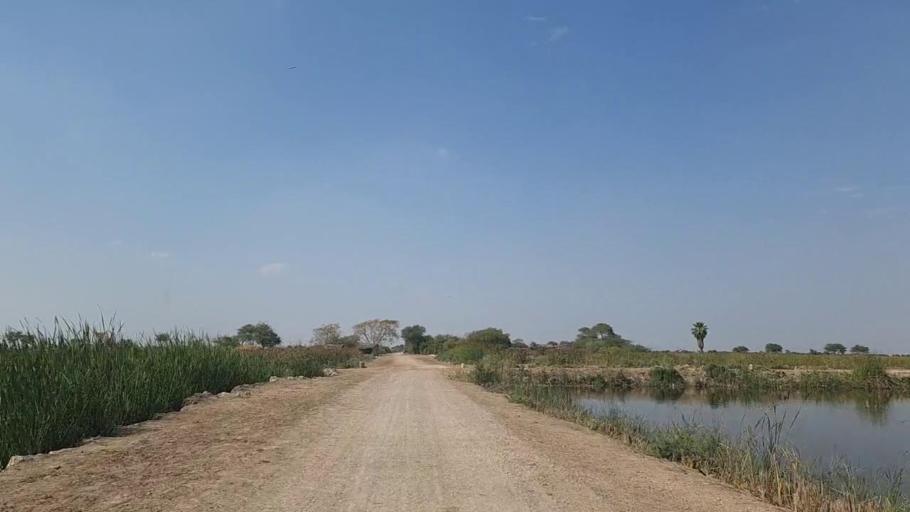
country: PK
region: Sindh
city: Jati
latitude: 24.5113
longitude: 68.2953
